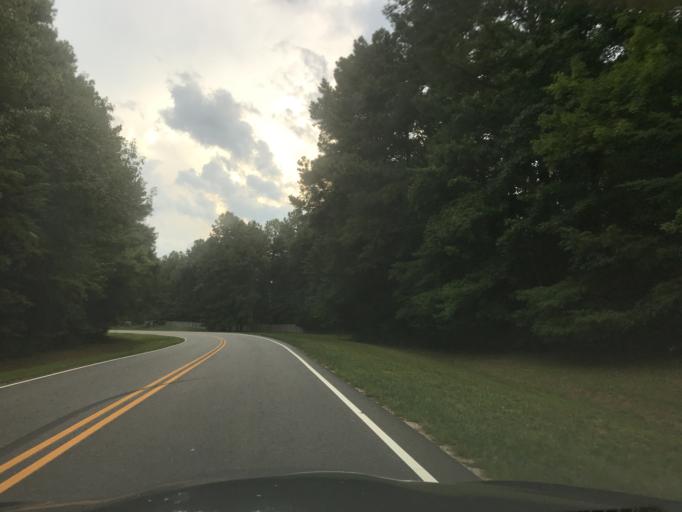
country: US
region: North Carolina
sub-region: Wake County
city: Wake Forest
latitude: 35.9224
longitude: -78.6026
